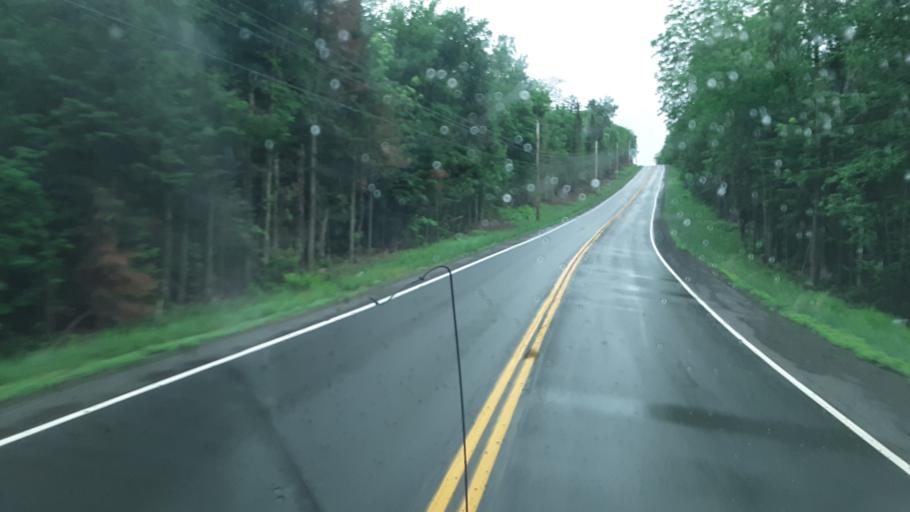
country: US
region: Maine
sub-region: Penobscot County
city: Patten
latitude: 46.1300
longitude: -68.3883
